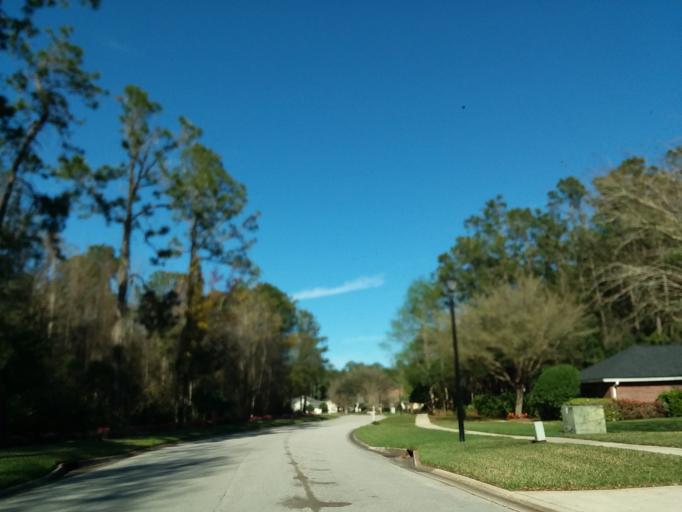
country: US
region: Florida
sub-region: Saint Johns County
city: Fruit Cove
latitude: 30.1958
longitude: -81.5432
